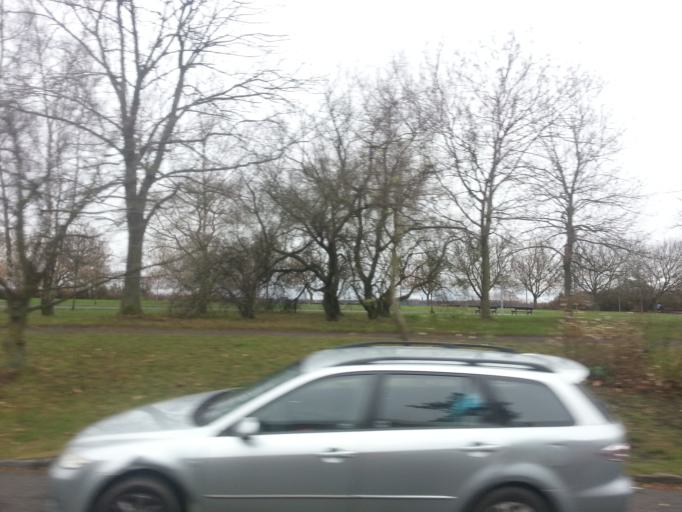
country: CZ
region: Praha
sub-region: Praha 1
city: Mala Strana
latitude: 50.0798
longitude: 14.3592
